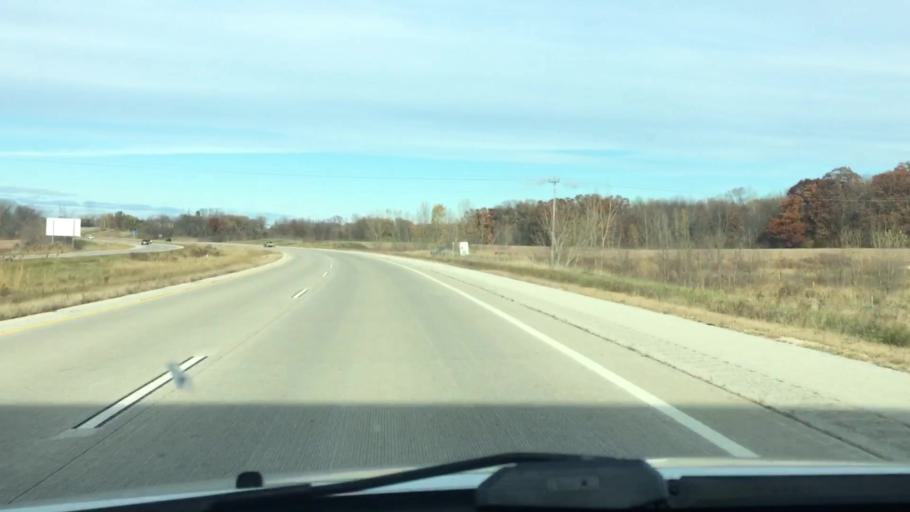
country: US
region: Wisconsin
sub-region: Kewaunee County
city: Luxemburg
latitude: 44.6387
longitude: -87.7544
